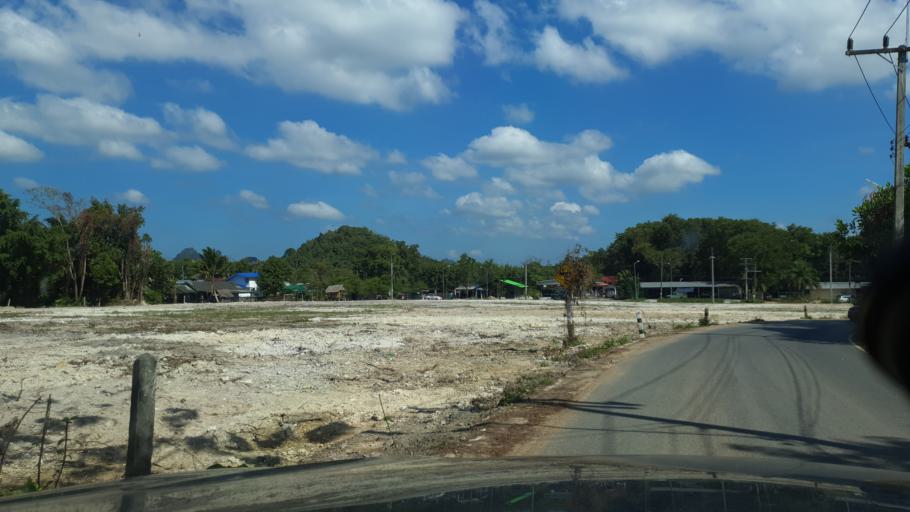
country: TH
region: Phangnga
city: Ban Ao Nang
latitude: 8.0335
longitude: 98.8574
